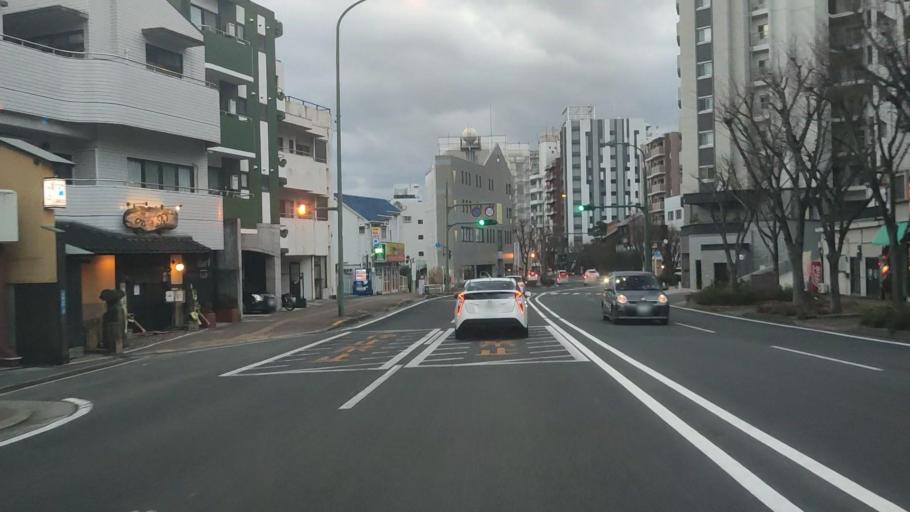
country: JP
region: Nagasaki
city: Nagasaki-shi
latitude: 32.7551
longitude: 129.8852
